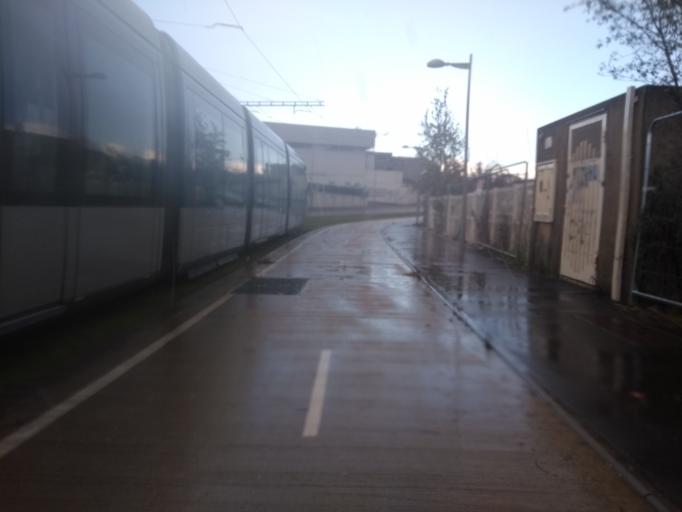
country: FR
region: Aquitaine
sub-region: Departement de la Gironde
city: Begles
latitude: 44.7888
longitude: -0.5651
